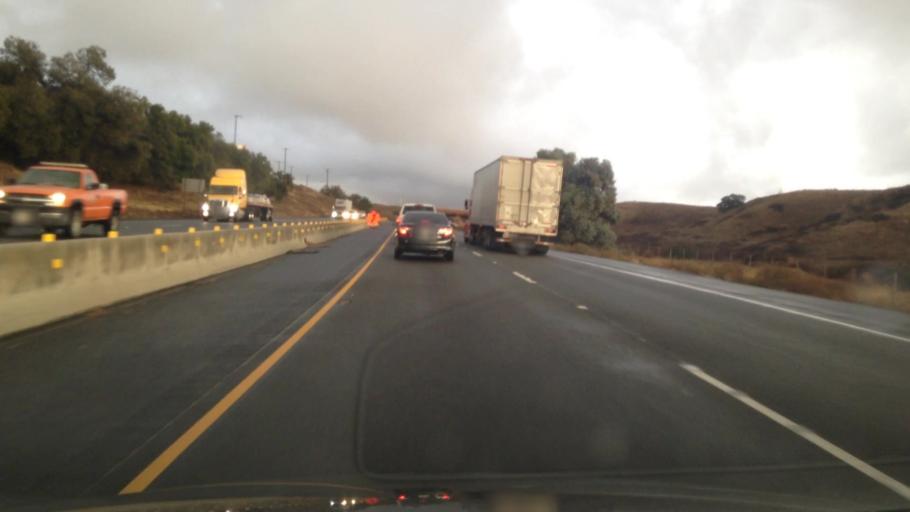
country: US
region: California
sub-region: Riverside County
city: Beaumont
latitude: 33.9329
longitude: -117.0233
